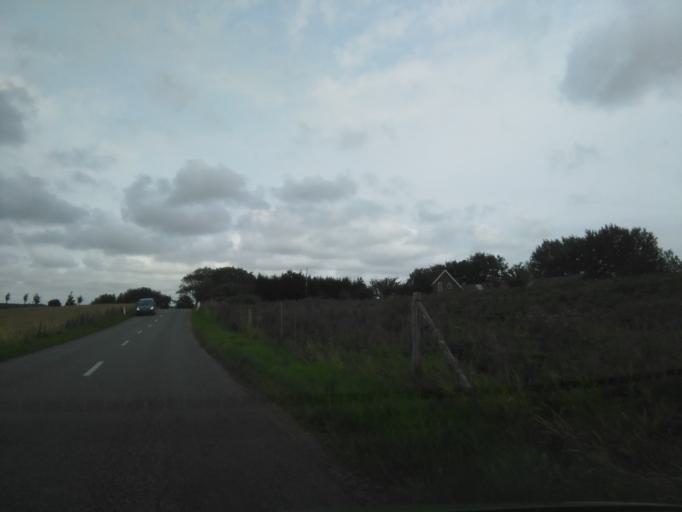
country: DK
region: Central Jutland
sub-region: Odder Kommune
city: Odder
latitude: 55.9522
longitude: 10.1100
